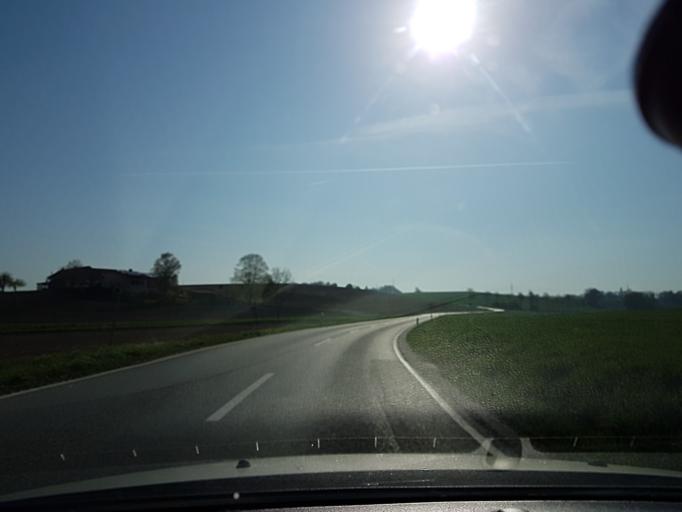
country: DE
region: Bavaria
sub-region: Lower Bavaria
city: Eging
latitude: 48.4524
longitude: 12.1885
